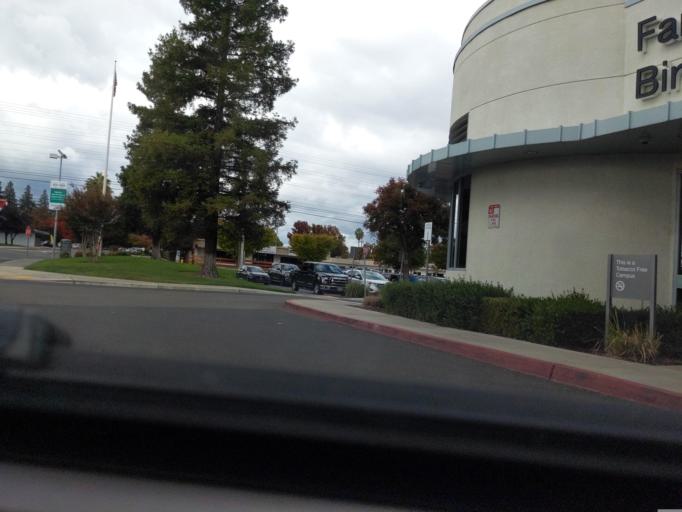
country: US
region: California
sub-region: Stanislaus County
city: Modesto
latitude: 37.6686
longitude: -120.9749
